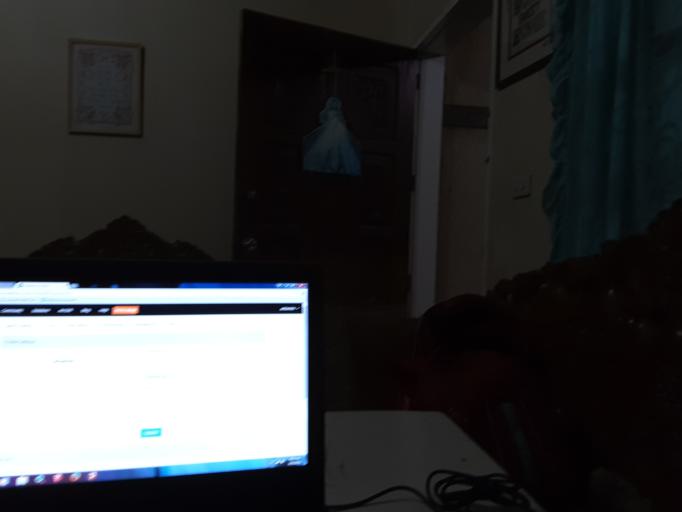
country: PH
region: Caraga
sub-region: Province of Agusan del Sur
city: Bah-Bah
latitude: 8.6041
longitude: 125.9148
